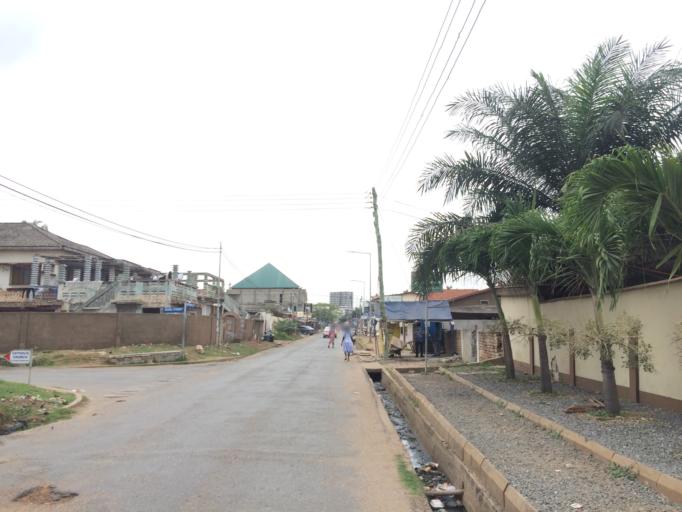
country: GH
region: Greater Accra
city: Accra
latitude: 5.5526
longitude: -0.1796
